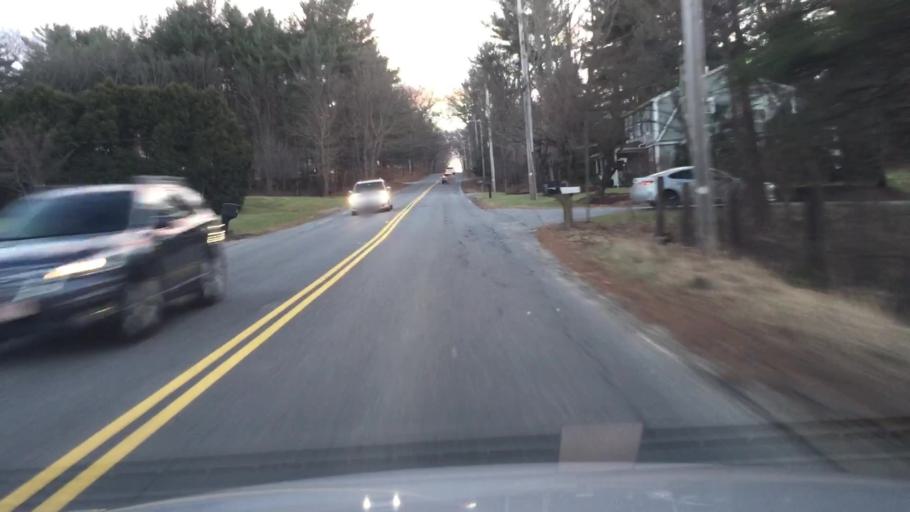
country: US
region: Massachusetts
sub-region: Worcester County
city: Sterling
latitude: 42.4137
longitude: -71.8015
